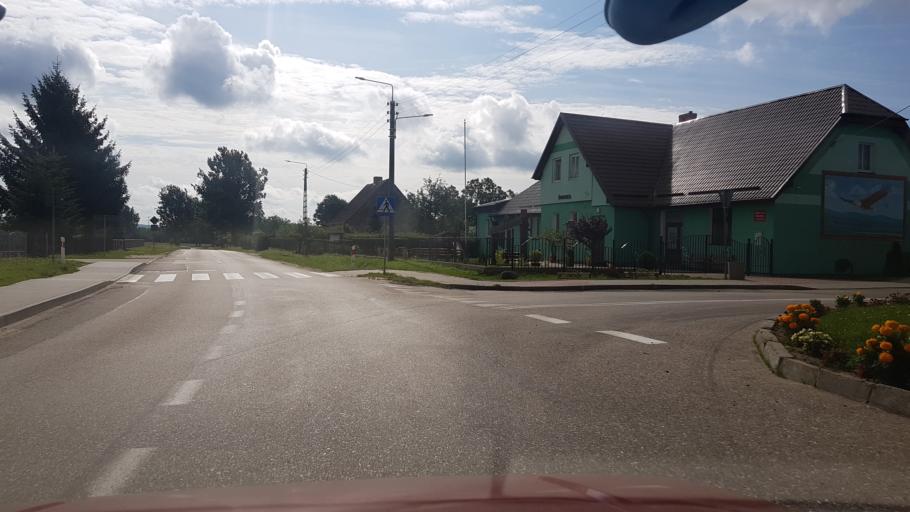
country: PL
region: Pomeranian Voivodeship
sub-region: Powiat bytowski
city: Miastko
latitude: 54.0825
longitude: 16.8540
